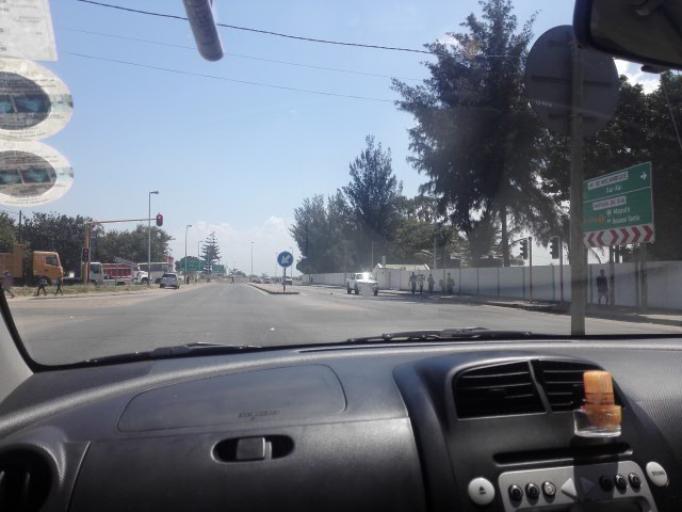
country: MZ
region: Maputo City
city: Maputo
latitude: -25.9384
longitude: 32.5468
